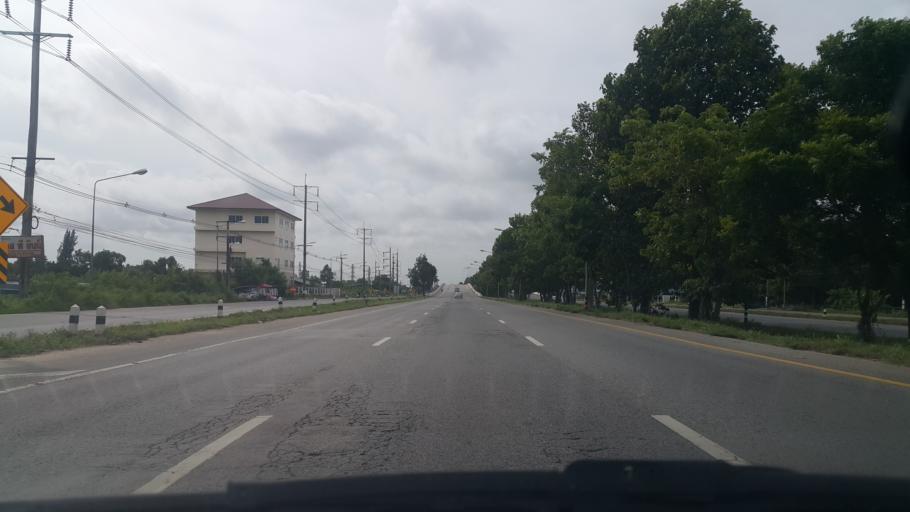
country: TH
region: Rayong
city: Rayong
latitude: 12.6799
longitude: 101.3012
